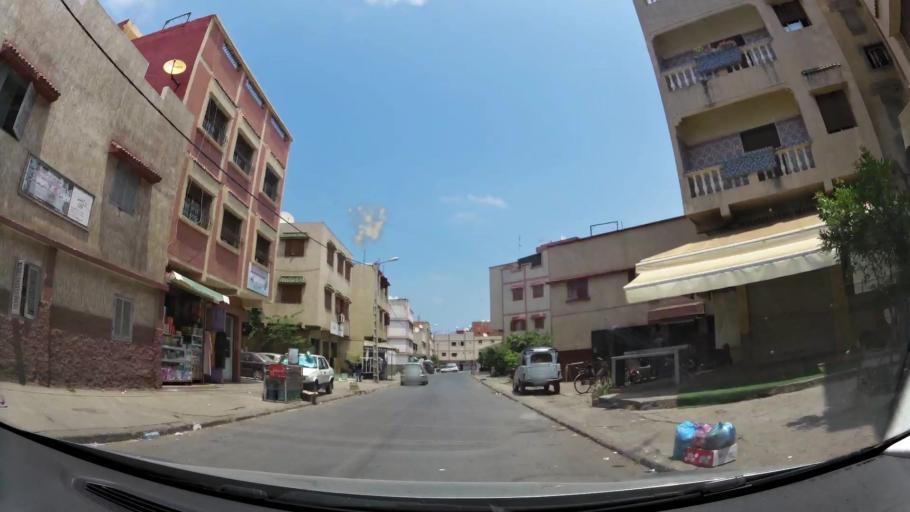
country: MA
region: Rabat-Sale-Zemmour-Zaer
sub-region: Skhirate-Temara
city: Temara
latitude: 33.9806
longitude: -6.8815
